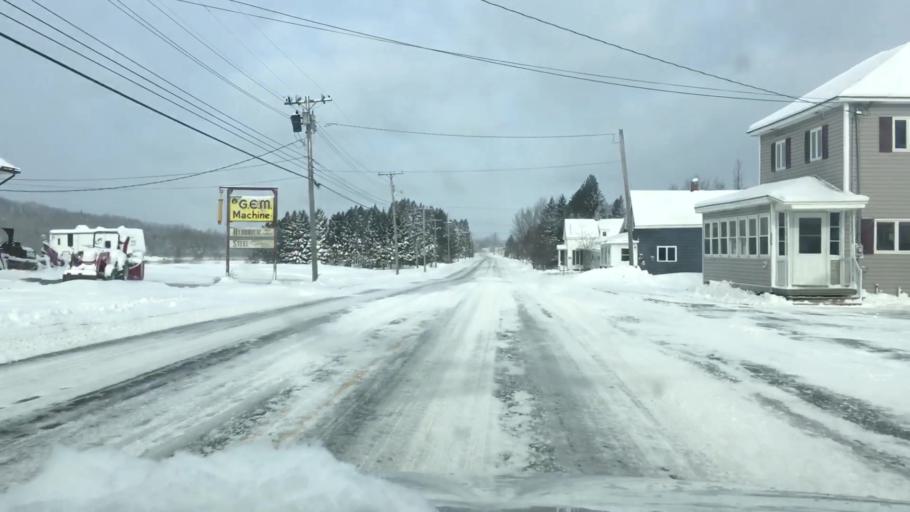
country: US
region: Maine
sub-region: Aroostook County
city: Van Buren
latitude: 47.1769
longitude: -67.9486
